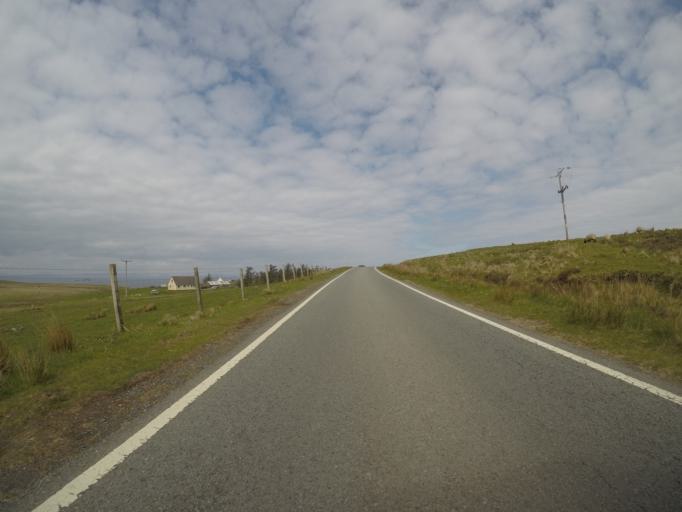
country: GB
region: Scotland
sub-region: Highland
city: Portree
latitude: 57.6527
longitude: -6.3800
